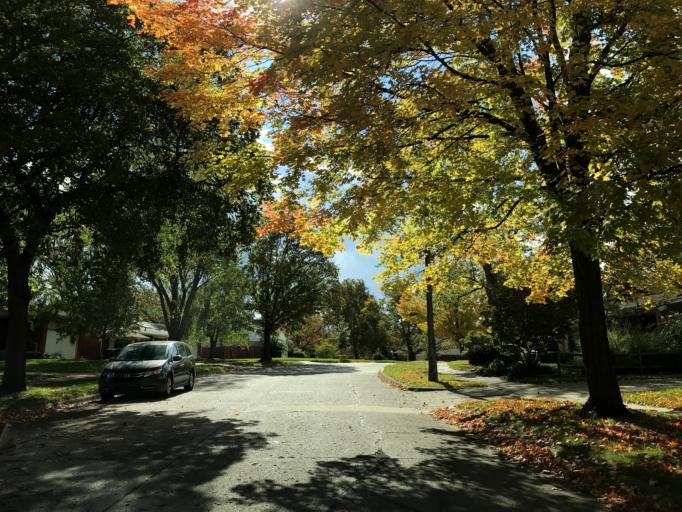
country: US
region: Michigan
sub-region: Washtenaw County
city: Ann Arbor
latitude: 42.2480
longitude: -83.7131
